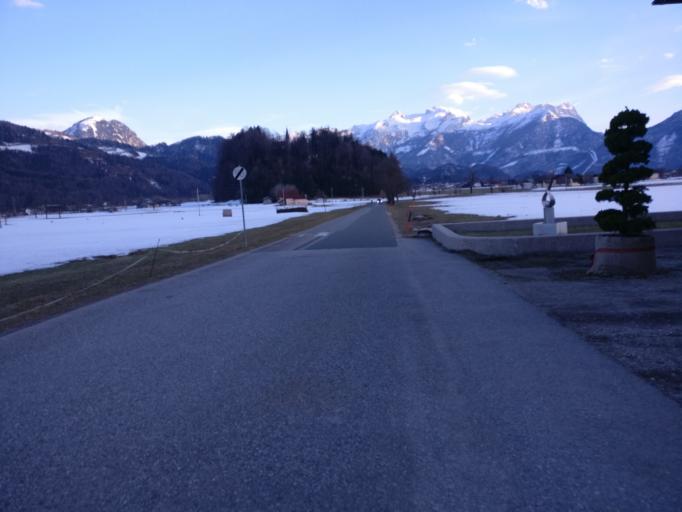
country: AT
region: Salzburg
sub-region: Politischer Bezirk Hallein
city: Kuchl
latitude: 47.6398
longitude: 13.1535
